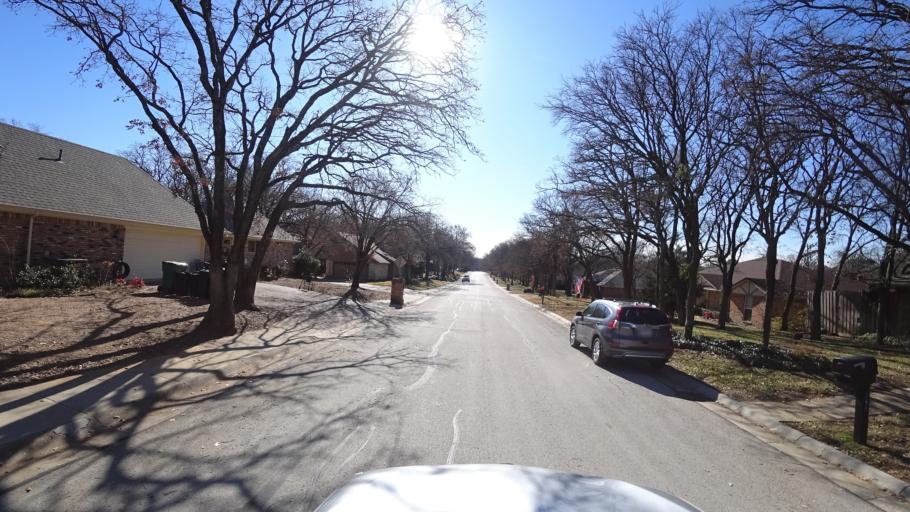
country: US
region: Texas
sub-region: Denton County
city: Lewisville
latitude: 33.0245
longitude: -97.0143
